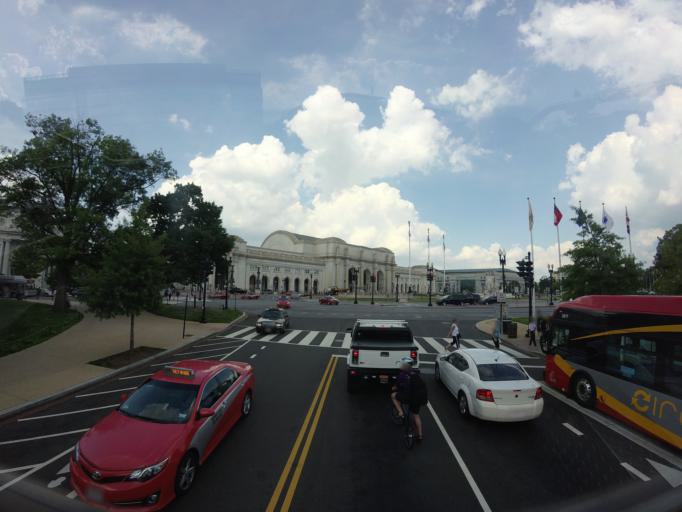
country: US
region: Washington, D.C.
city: Washington, D.C.
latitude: 38.8965
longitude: -77.0081
